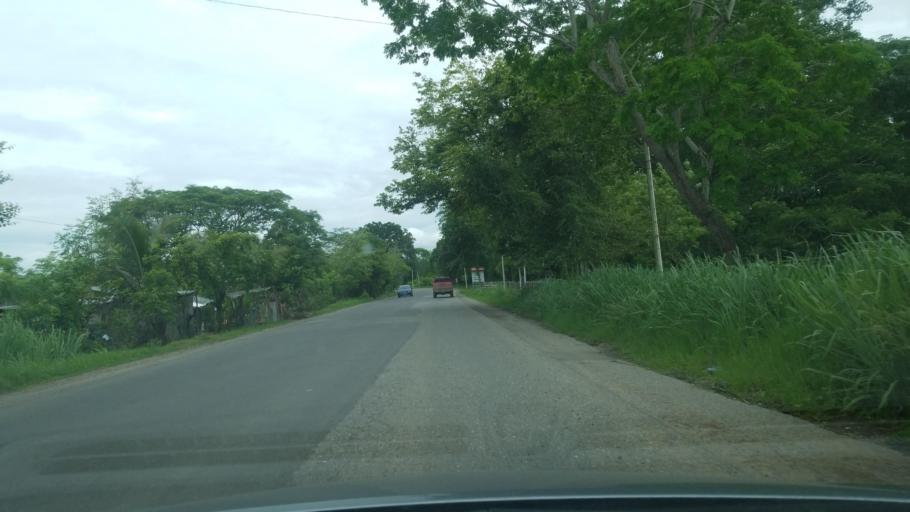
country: HN
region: Santa Barbara
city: La Flecha
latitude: 15.2986
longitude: -88.4718
